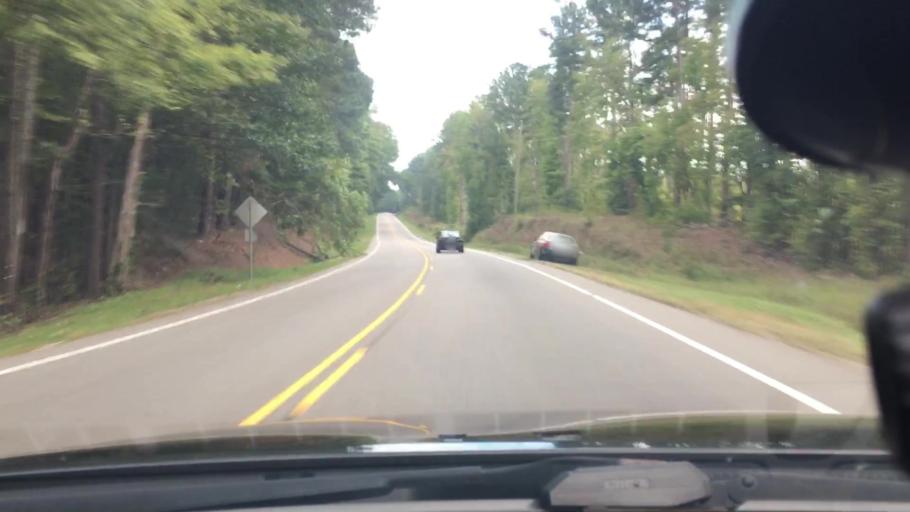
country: US
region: North Carolina
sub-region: Moore County
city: Carthage
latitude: 35.3616
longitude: -79.4405
